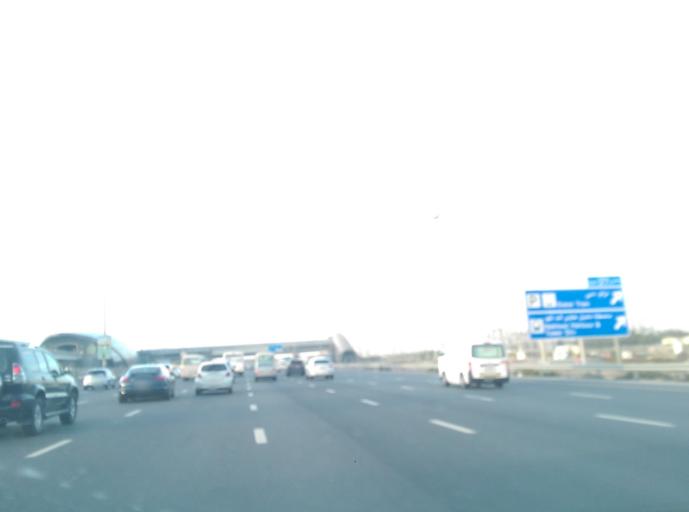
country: AE
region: Dubai
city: Dubai
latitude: 25.0603
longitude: 55.1286
